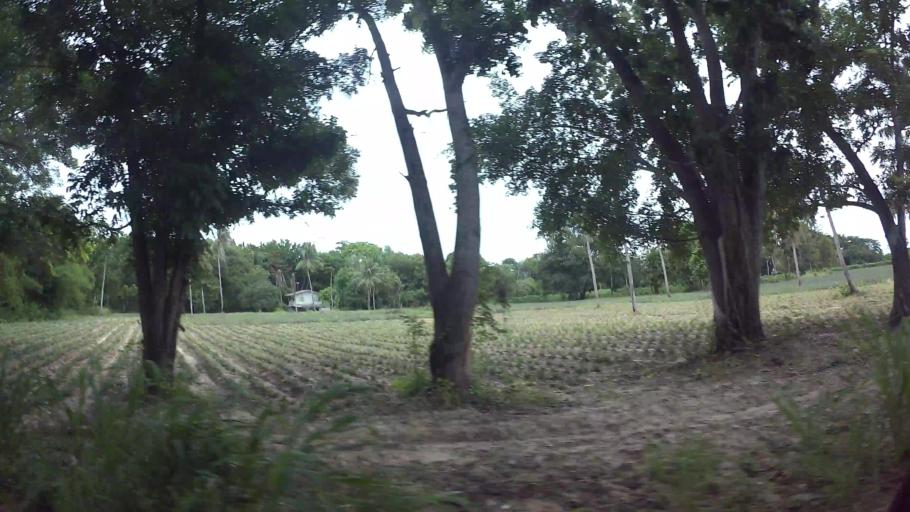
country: TH
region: Chon Buri
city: Si Racha
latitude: 13.1780
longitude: 100.9766
